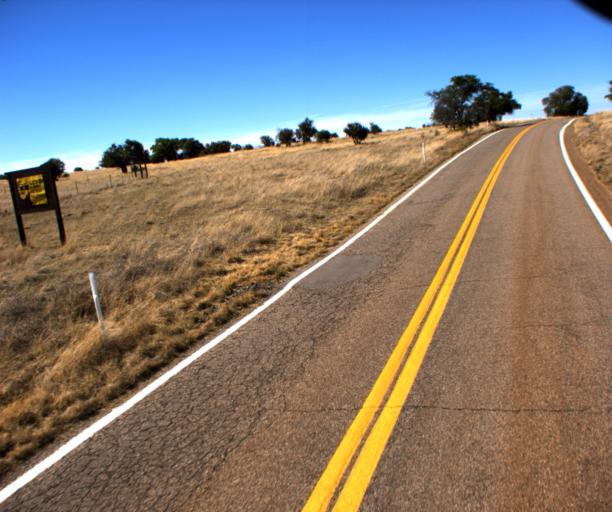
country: US
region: Arizona
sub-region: Cochise County
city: Huachuca City
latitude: 31.5682
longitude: -110.5600
